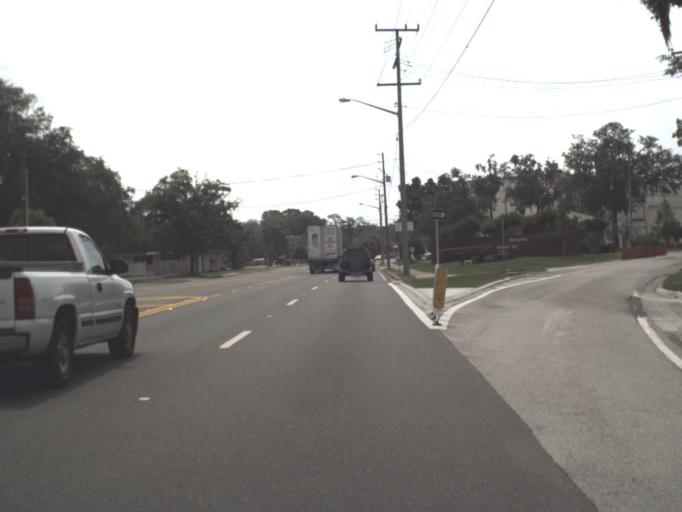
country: US
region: Florida
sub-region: Clay County
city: Green Cove Springs
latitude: 30.0053
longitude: -81.6890
